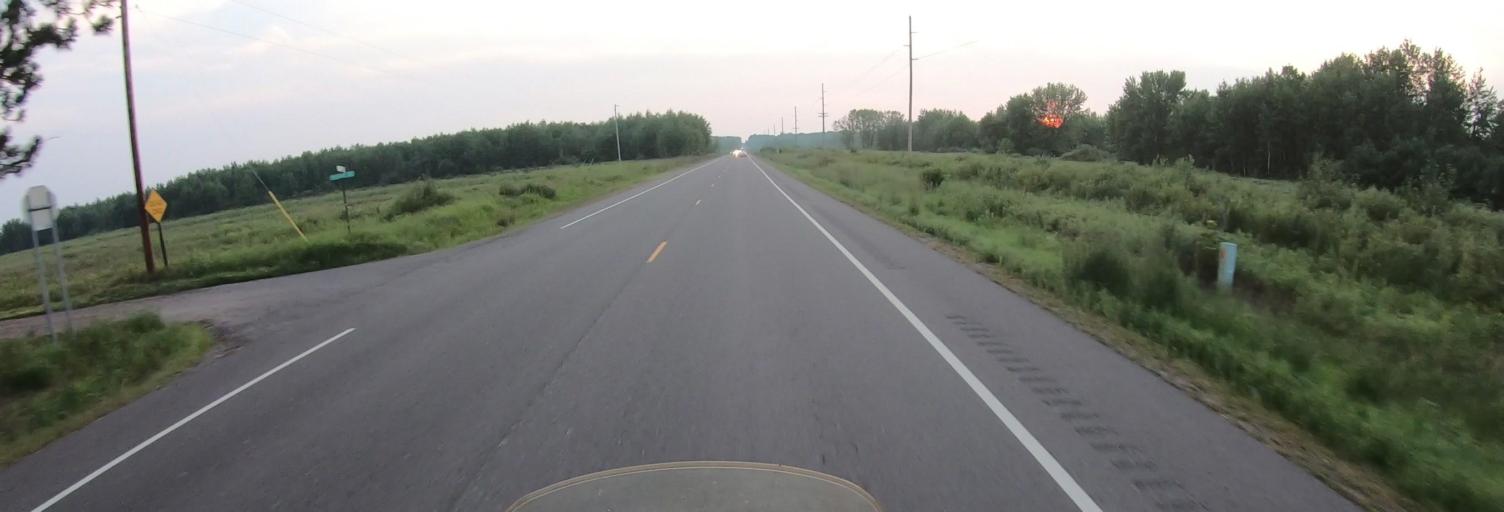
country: US
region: Wisconsin
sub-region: Burnett County
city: Grantsburg
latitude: 45.7735
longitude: -92.8214
